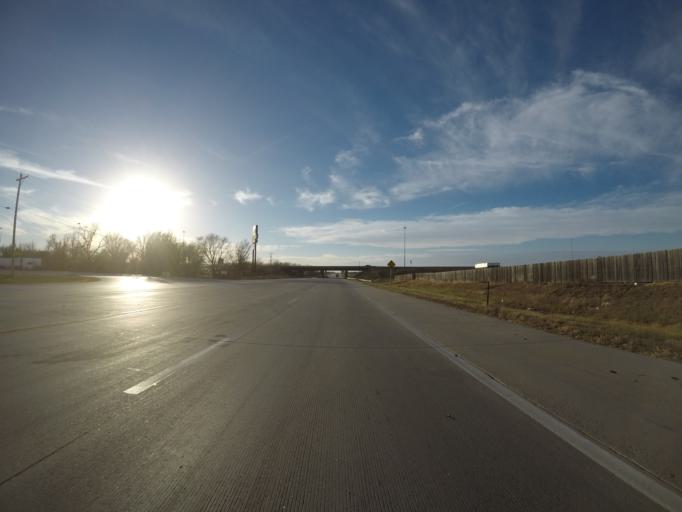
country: US
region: Kansas
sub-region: Lyon County
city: Emporia
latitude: 38.4123
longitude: -96.2374
